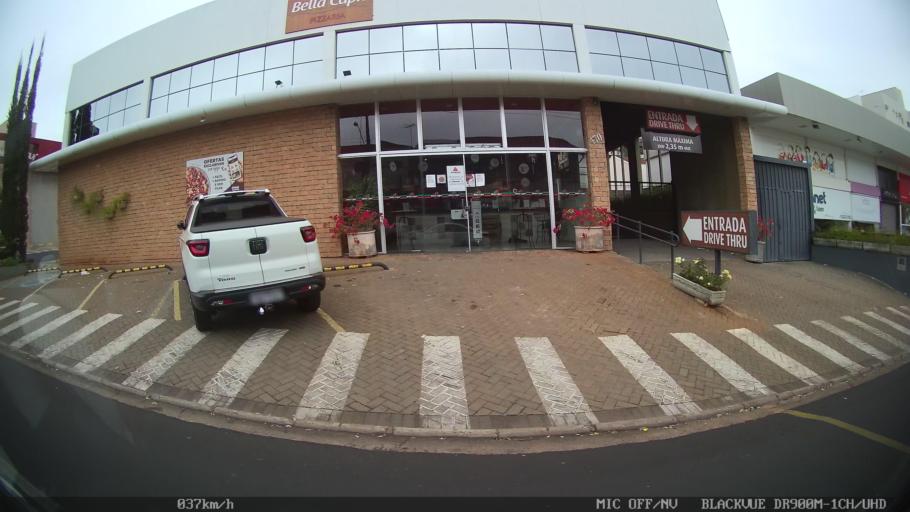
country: BR
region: Sao Paulo
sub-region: Sao Jose Do Rio Preto
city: Sao Jose do Rio Preto
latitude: -20.8353
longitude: -49.3889
